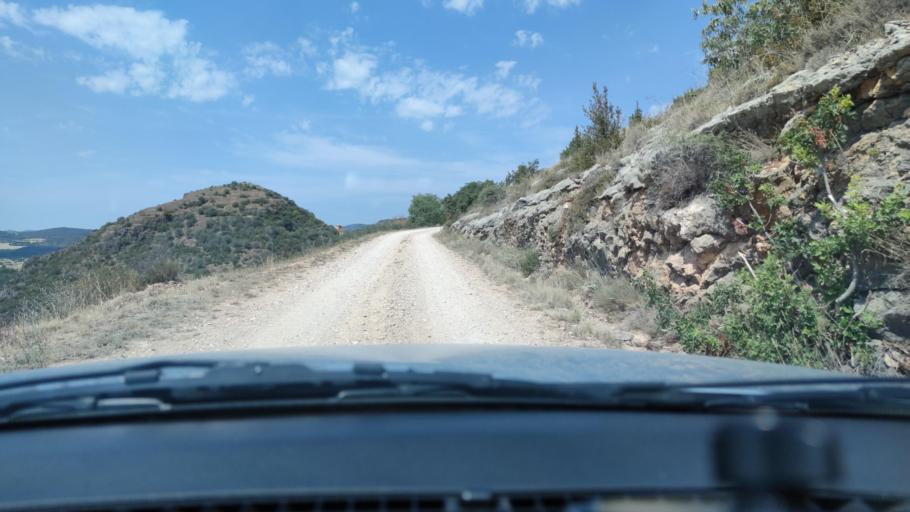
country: ES
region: Catalonia
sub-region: Provincia de Lleida
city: Ager
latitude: 41.9277
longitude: 0.8091
